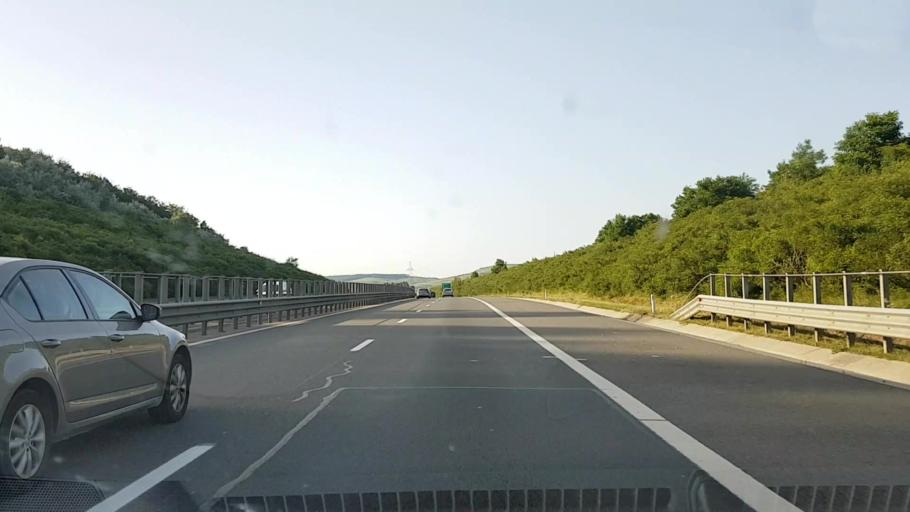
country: RO
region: Cluj
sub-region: Comuna Floresti
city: Luna de Sus
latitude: 46.7379
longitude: 23.4193
